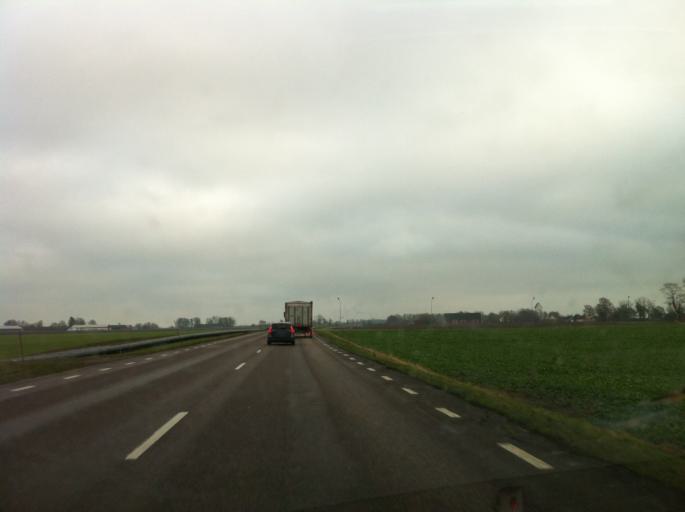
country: SE
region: Skane
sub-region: Kavlinge Kommun
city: Kaevlinge
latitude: 55.7967
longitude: 13.1879
